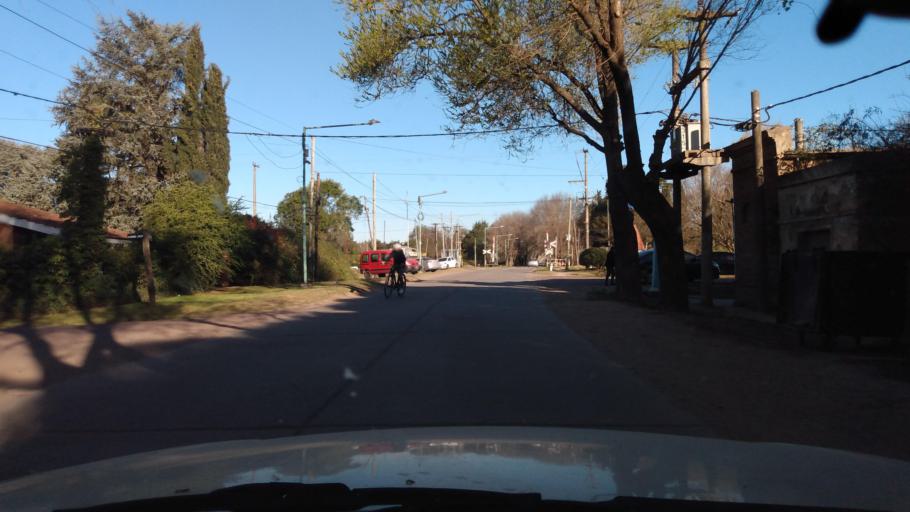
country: AR
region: Buenos Aires
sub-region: Partido de Lujan
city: Lujan
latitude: -34.6262
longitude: -59.2531
